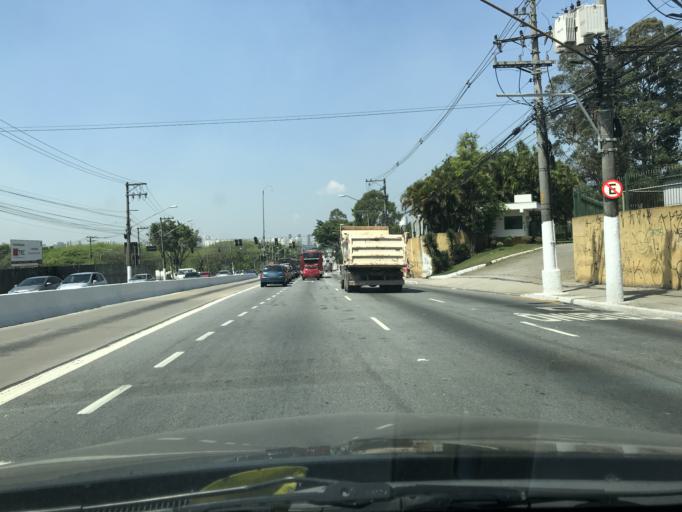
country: BR
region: Sao Paulo
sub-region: Taboao Da Serra
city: Taboao da Serra
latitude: -23.6674
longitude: -46.7284
